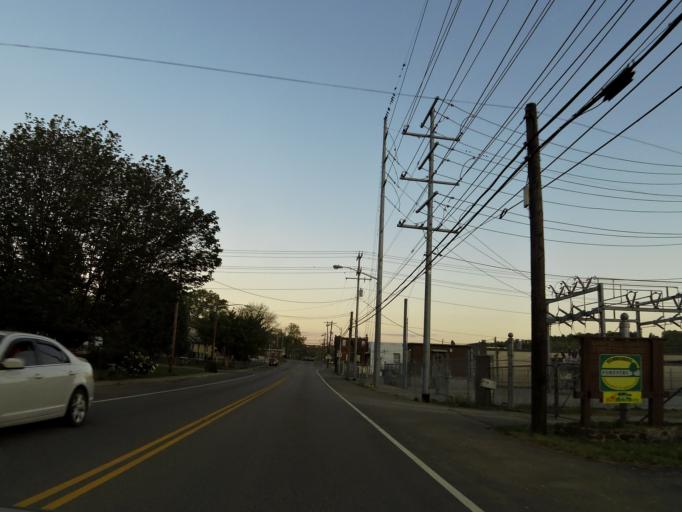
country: US
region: Tennessee
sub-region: Campbell County
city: LaFollette
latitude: 36.3839
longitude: -84.1216
